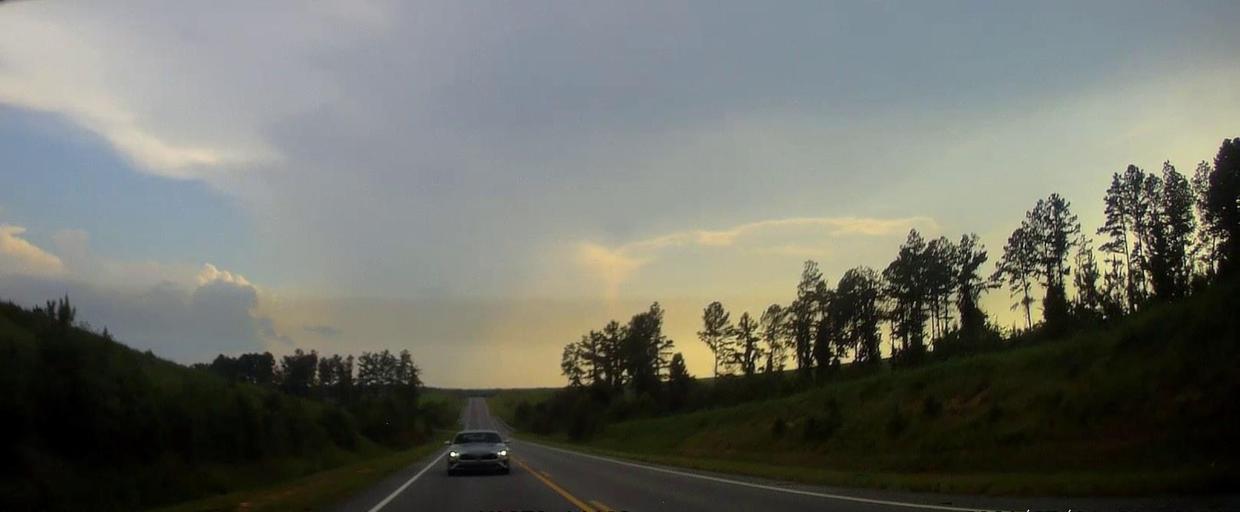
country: US
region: Georgia
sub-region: Laurens County
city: East Dublin
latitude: 32.6201
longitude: -82.8825
